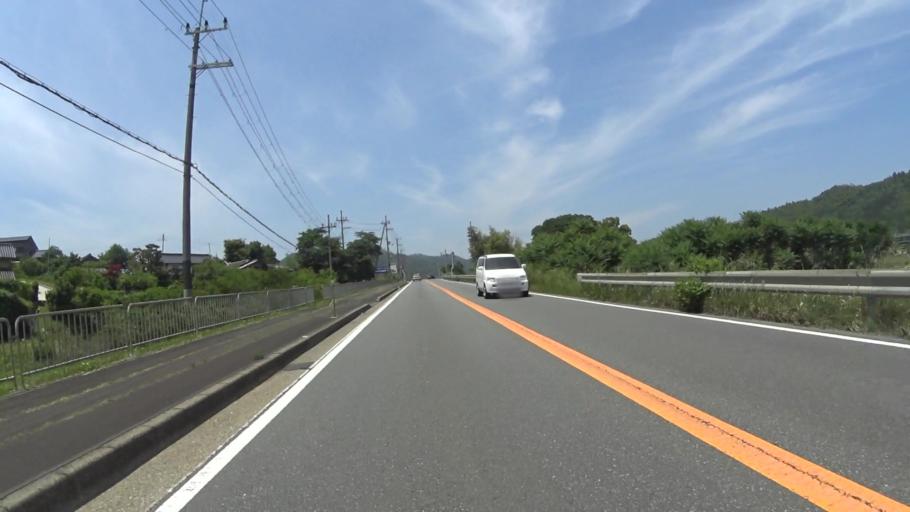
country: JP
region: Kyoto
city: Ayabe
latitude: 35.2471
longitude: 135.2154
